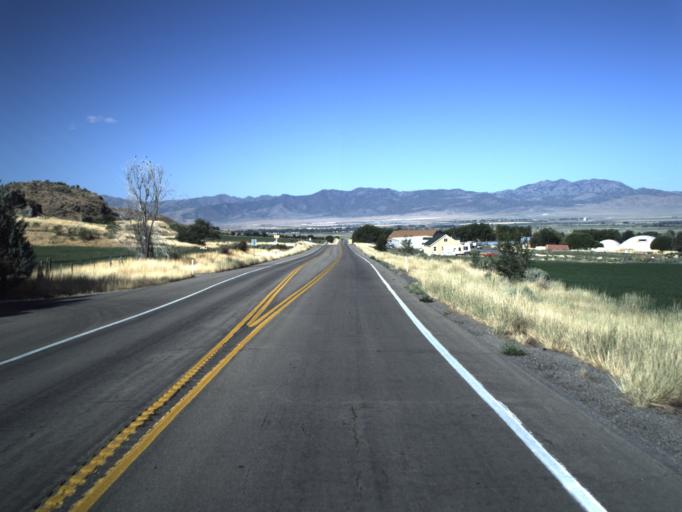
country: US
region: Utah
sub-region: Utah County
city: Genola
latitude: 39.9820
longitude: -111.8290
